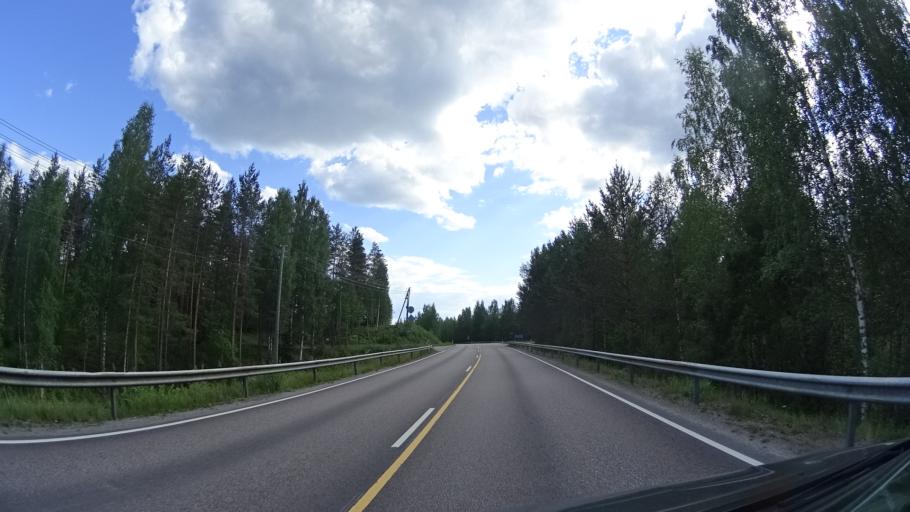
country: FI
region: Southern Savonia
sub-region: Savonlinna
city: Punkaharju
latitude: 61.6807
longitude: 29.4145
